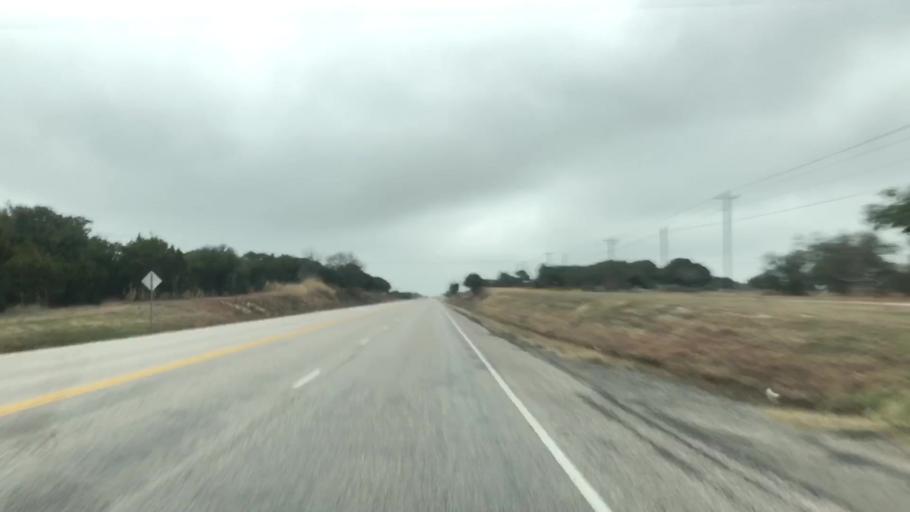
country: US
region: Texas
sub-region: Burnet County
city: Burnet
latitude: 30.8250
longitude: -98.2384
